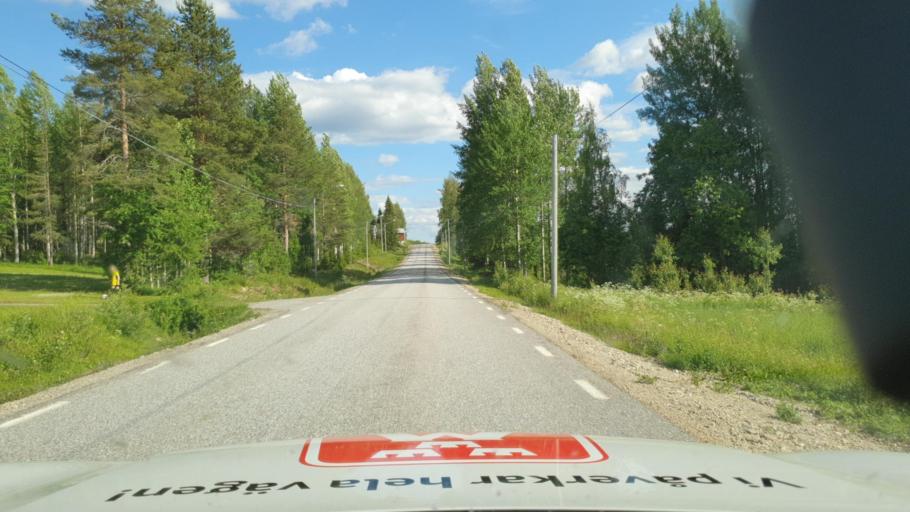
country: SE
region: Vaesterbotten
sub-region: Skelleftea Kommun
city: Langsele
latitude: 64.7496
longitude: 19.9438
